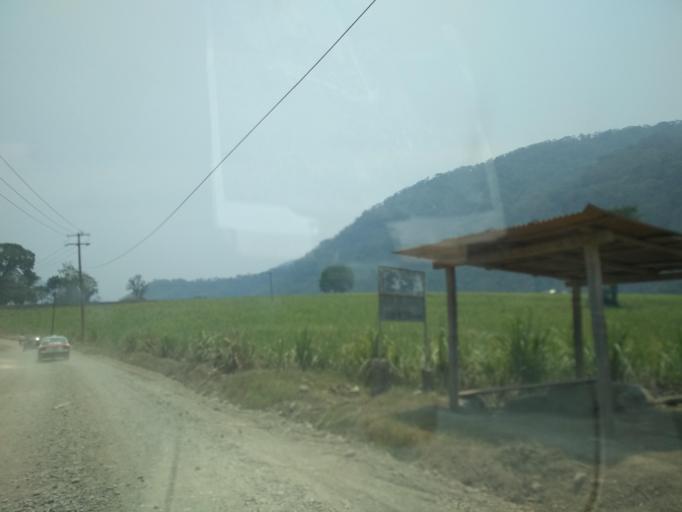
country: MX
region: Veracruz
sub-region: Tezonapa
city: Laguna Chica (Pueblo Nuevo)
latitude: 18.5624
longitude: -96.7233
